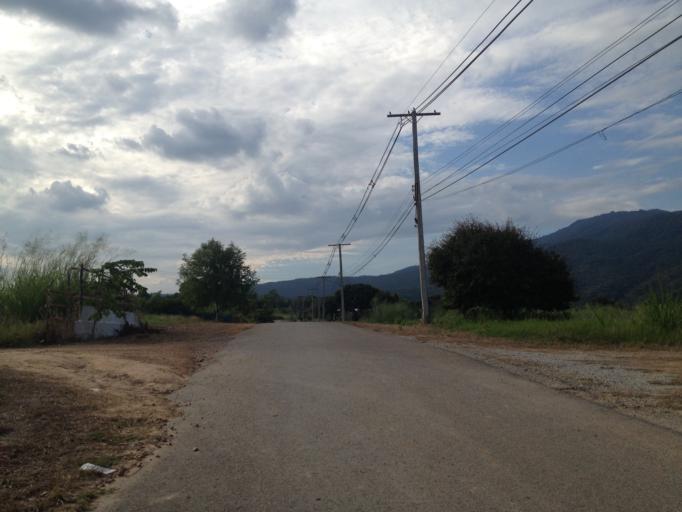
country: TH
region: Chiang Mai
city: Chiang Mai
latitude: 18.7574
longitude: 98.9379
